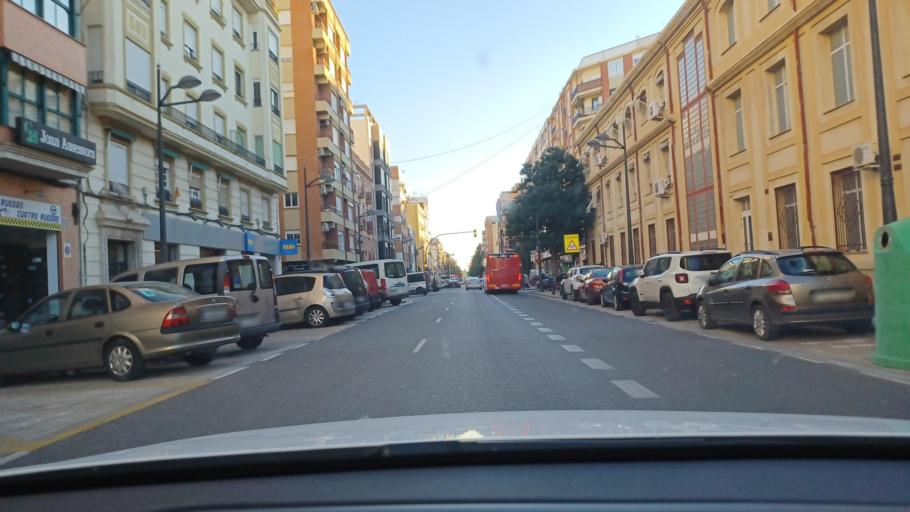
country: ES
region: Valencia
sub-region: Provincia de Valencia
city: Valencia
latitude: 39.4584
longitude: -0.3891
